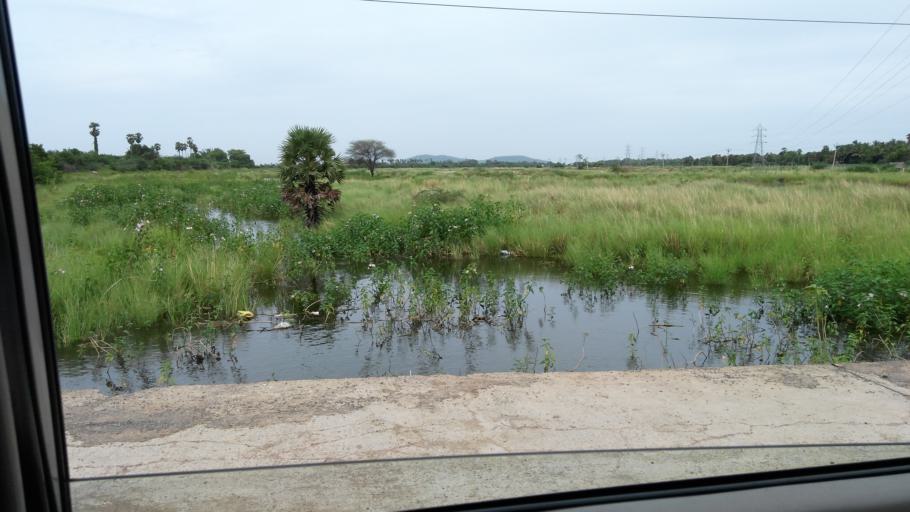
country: IN
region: Tamil Nadu
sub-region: Kancheepuram
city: Vandalur
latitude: 12.9250
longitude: 80.0204
